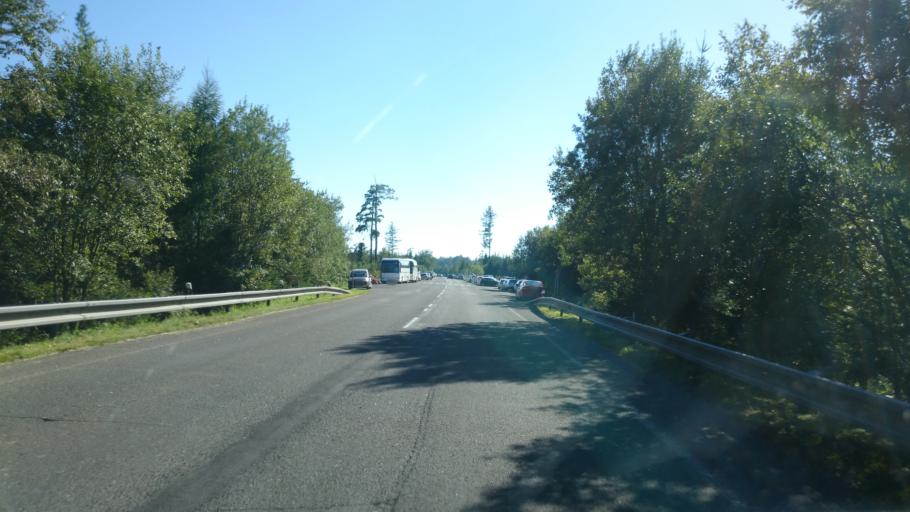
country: SK
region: Presovsky
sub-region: Okres Poprad
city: Nova Lesna
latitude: 49.1889
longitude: 20.2940
